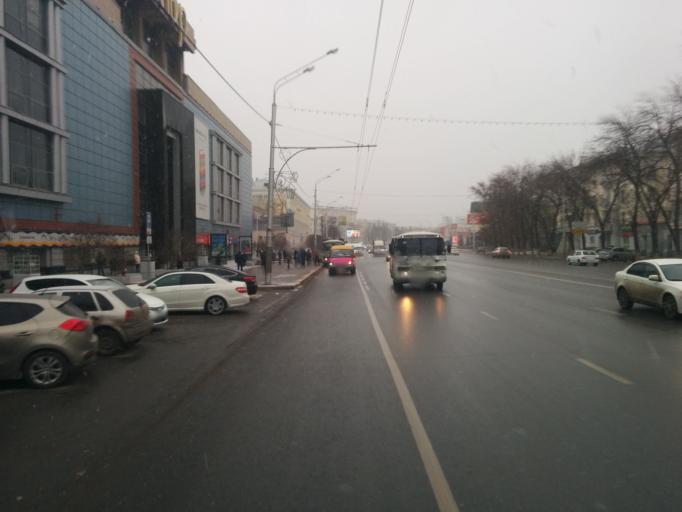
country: RU
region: Bashkortostan
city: Ufa
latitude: 54.7414
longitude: 55.9871
